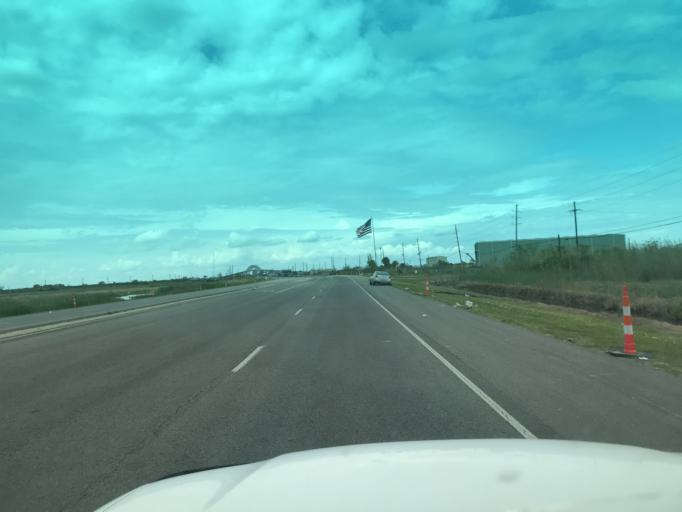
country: US
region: Louisiana
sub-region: Saint Bernard Parish
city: Chalmette
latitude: 29.9755
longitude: -89.9474
